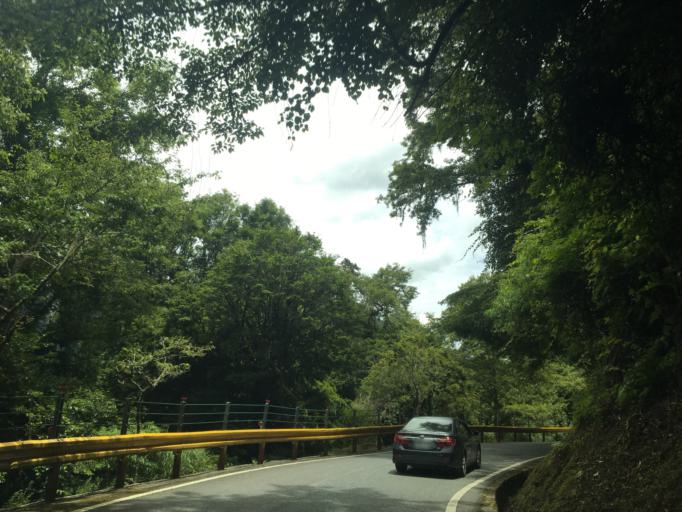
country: TW
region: Taiwan
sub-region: Hualien
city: Hualian
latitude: 24.1800
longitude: 121.3908
